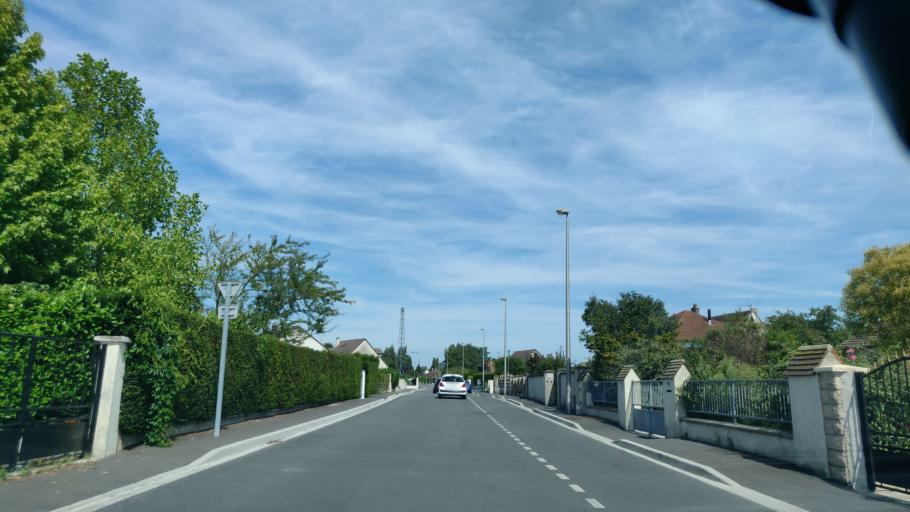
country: FR
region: Picardie
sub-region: Departement de l'Oise
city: Pont-Sainte-Maxence
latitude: 49.3093
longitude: 2.6175
